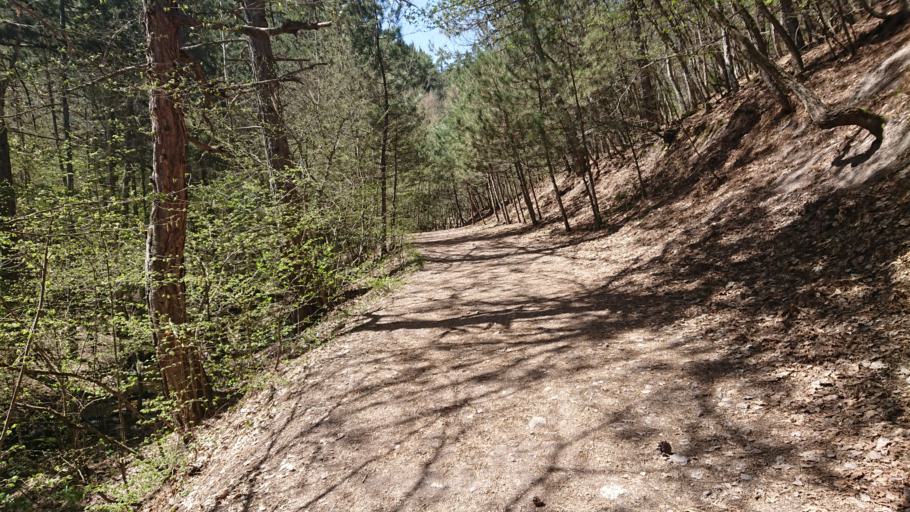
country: TR
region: Kuetahya
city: Sabuncu
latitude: 39.5091
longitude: 30.4199
